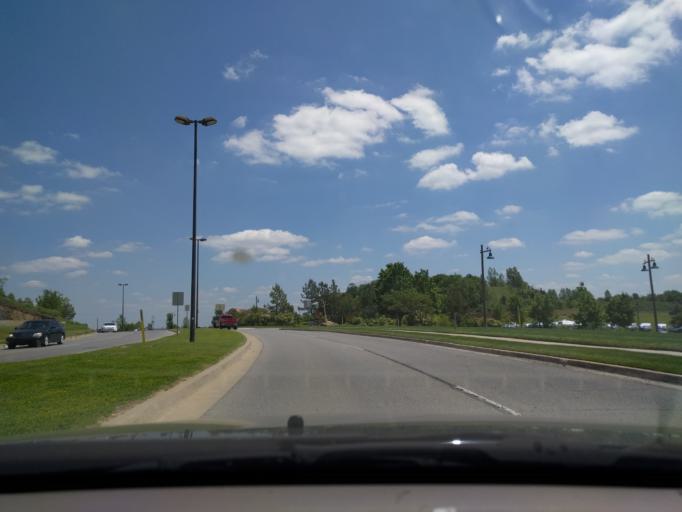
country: US
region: Oklahoma
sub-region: Tulsa County
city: Broken Arrow
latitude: 36.0725
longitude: -95.7926
